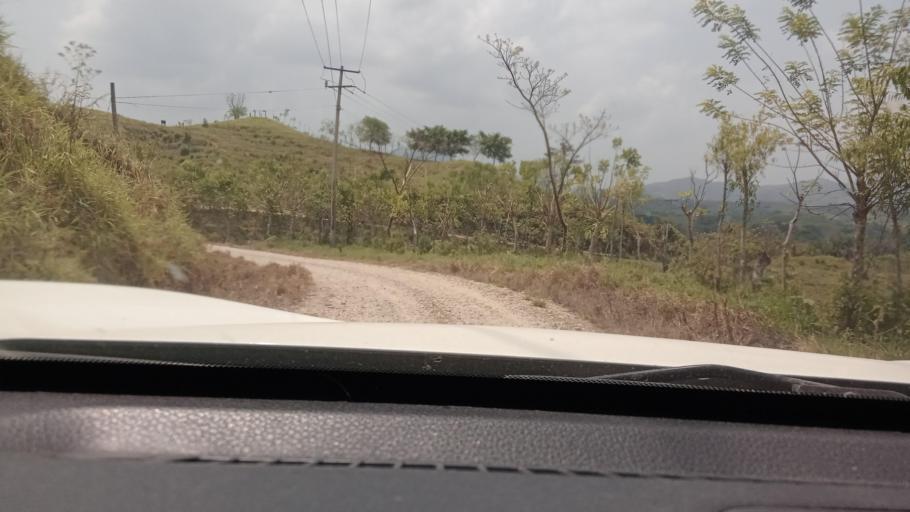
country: MX
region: Tabasco
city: Chontalpa
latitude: 17.5719
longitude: -93.7098
